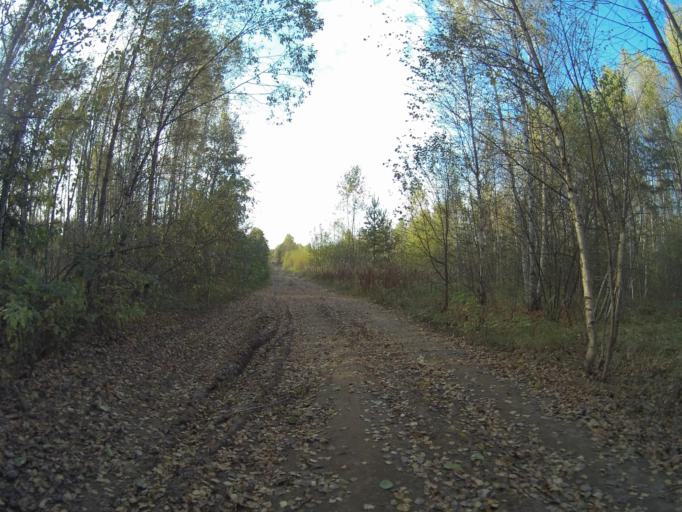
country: RU
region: Vladimir
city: Urshel'skiy
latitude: 55.7969
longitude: 40.0640
